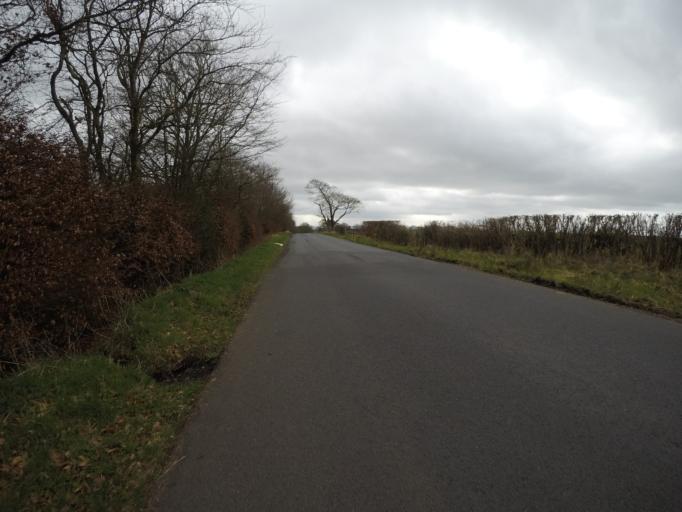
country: GB
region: Scotland
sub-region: East Ayrshire
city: Stewarton
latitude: 55.6811
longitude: -4.4410
